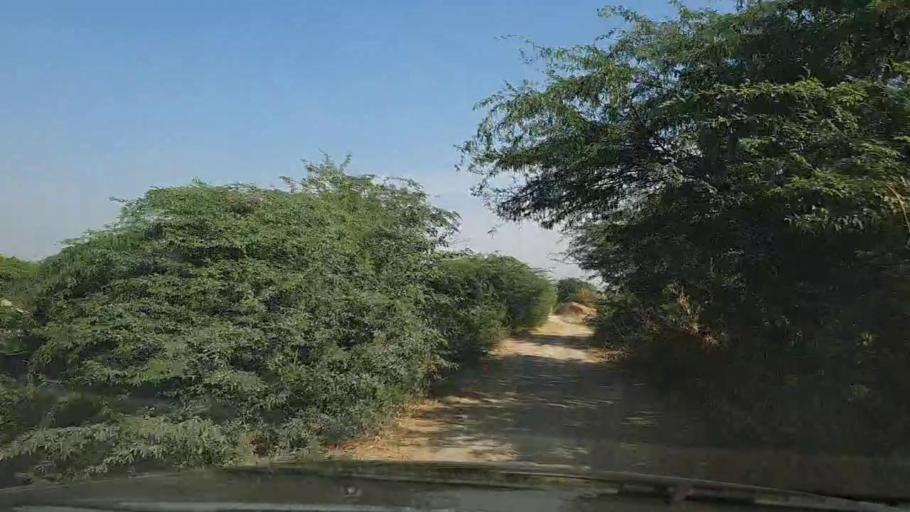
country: PK
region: Sindh
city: Thatta
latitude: 24.7114
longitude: 67.7855
